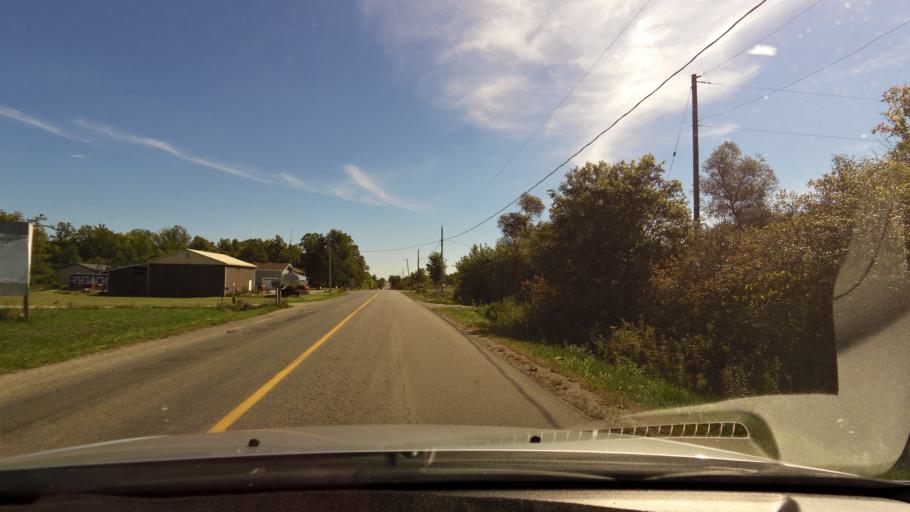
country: CA
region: Ontario
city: Ancaster
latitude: 43.0673
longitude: -80.0580
